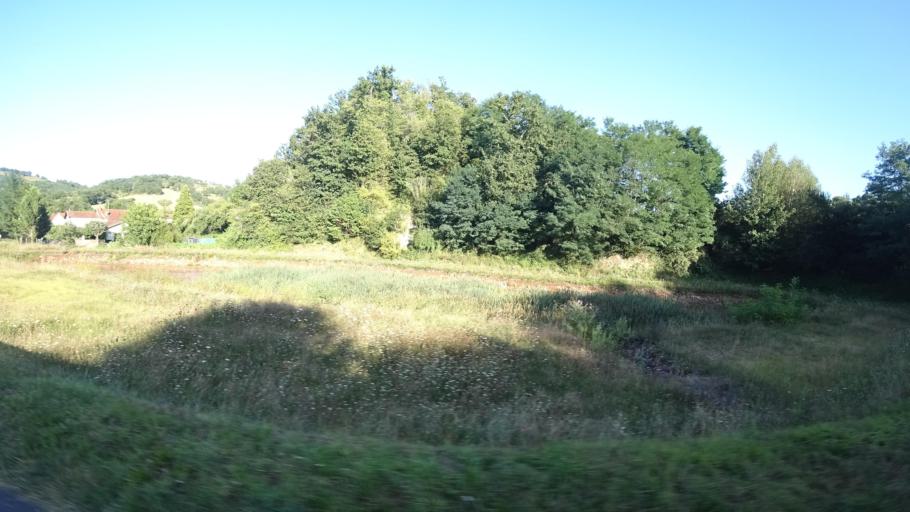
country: FR
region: Midi-Pyrenees
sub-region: Departement de l'Aveyron
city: Firmi
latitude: 44.5345
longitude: 2.3171
